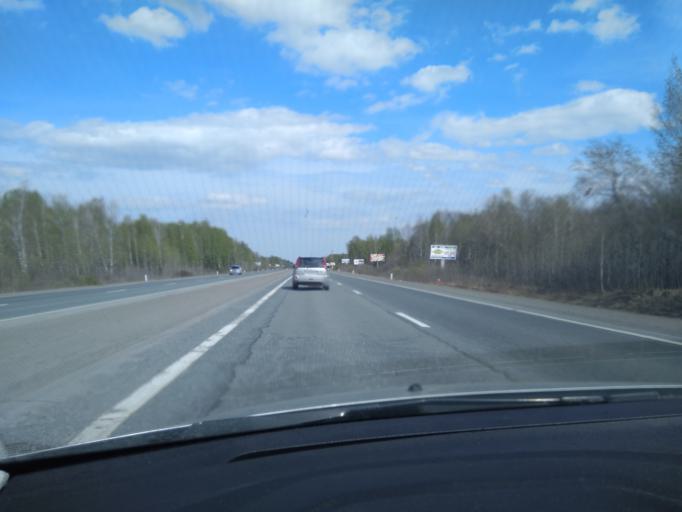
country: RU
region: Tjumen
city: Moskovskiy
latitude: 57.1097
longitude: 65.3803
